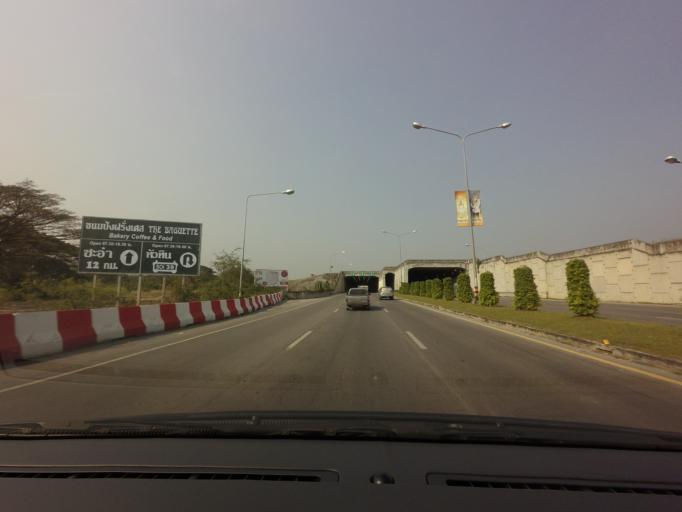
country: TH
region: Prachuap Khiri Khan
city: Hua Hin
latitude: 12.6405
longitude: 99.9487
